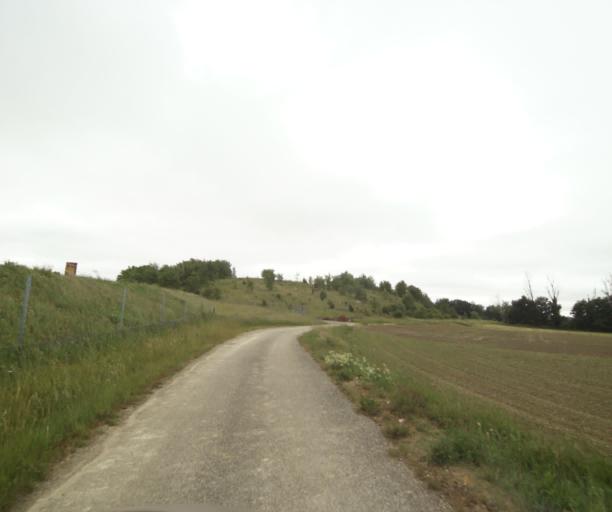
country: FR
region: Rhone-Alpes
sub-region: Departement de l'Ain
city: Tramoyes
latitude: 45.8594
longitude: 4.9504
